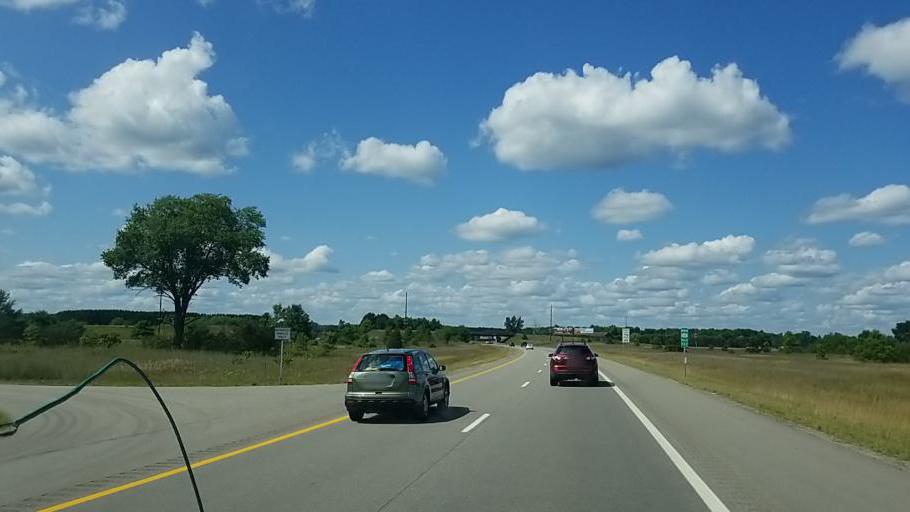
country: US
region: Michigan
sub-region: Mecosta County
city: Big Rapids
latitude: 43.5936
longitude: -85.4875
